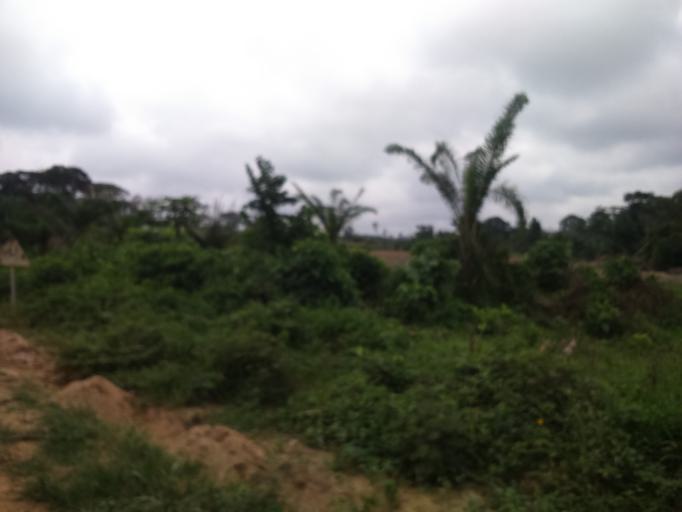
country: CI
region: Agneby
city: Agboville
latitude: 6.0536
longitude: -4.1009
